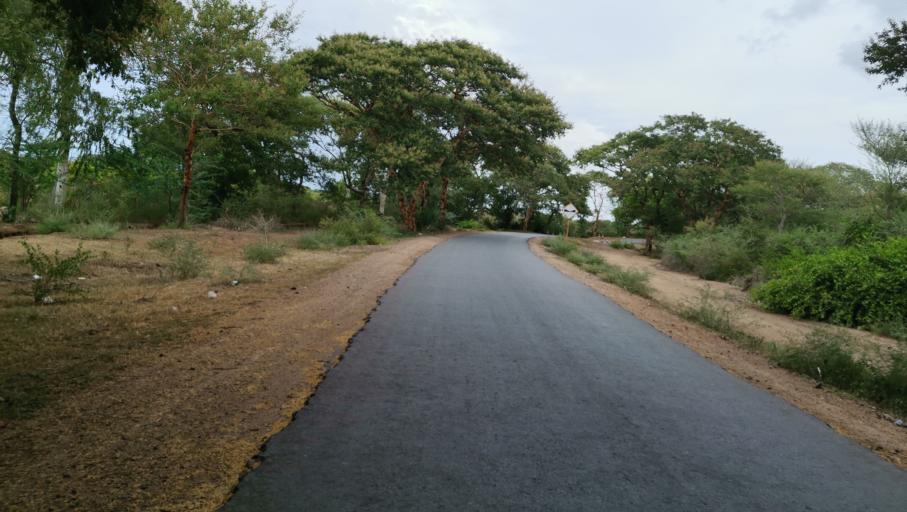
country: MM
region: Mandalay
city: Myingyan
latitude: 21.8499
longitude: 95.4308
